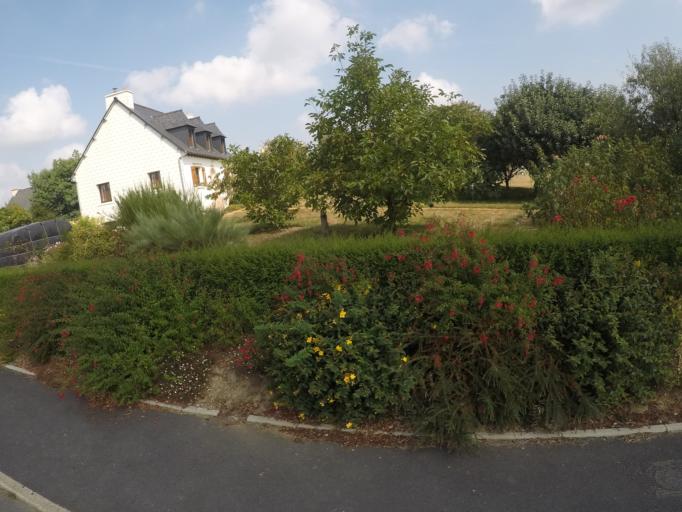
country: FR
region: Brittany
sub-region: Departement des Cotes-d'Armor
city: Saint-Donan
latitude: 48.5035
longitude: -2.9140
